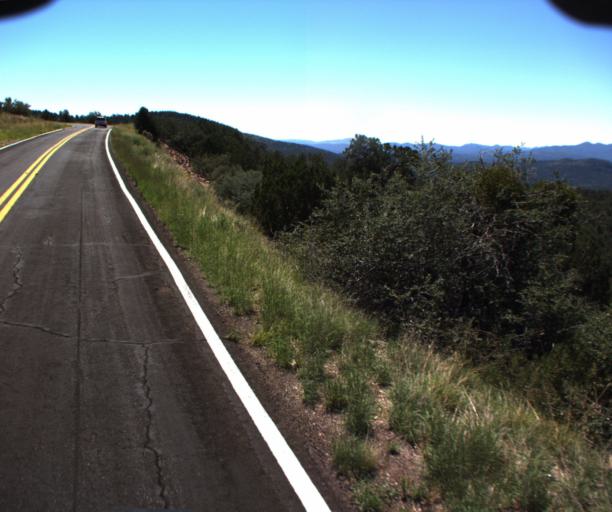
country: US
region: Arizona
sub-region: Greenlee County
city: Morenci
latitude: 33.4014
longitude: -109.3483
